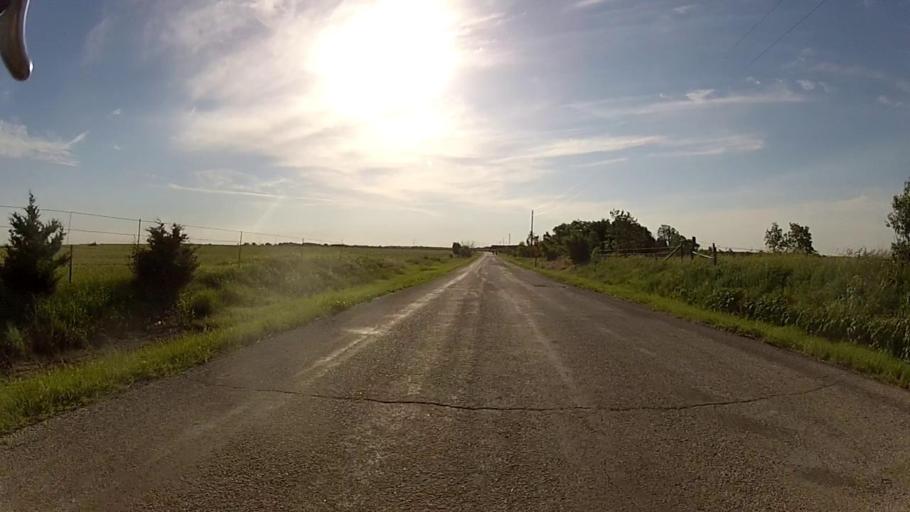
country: US
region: Kansas
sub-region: Cowley County
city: Arkansas City
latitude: 37.0485
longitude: -96.8276
